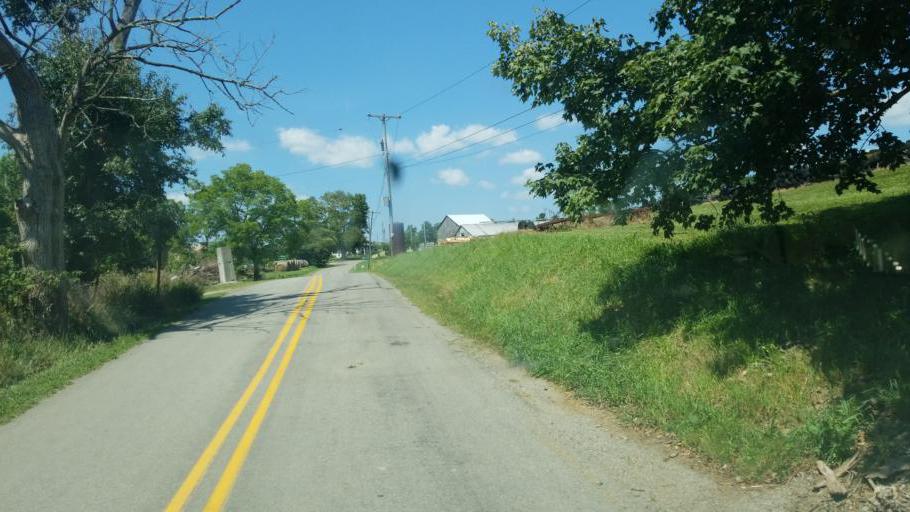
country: US
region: Pennsylvania
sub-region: Clarion County
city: Knox
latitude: 41.1981
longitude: -79.5534
